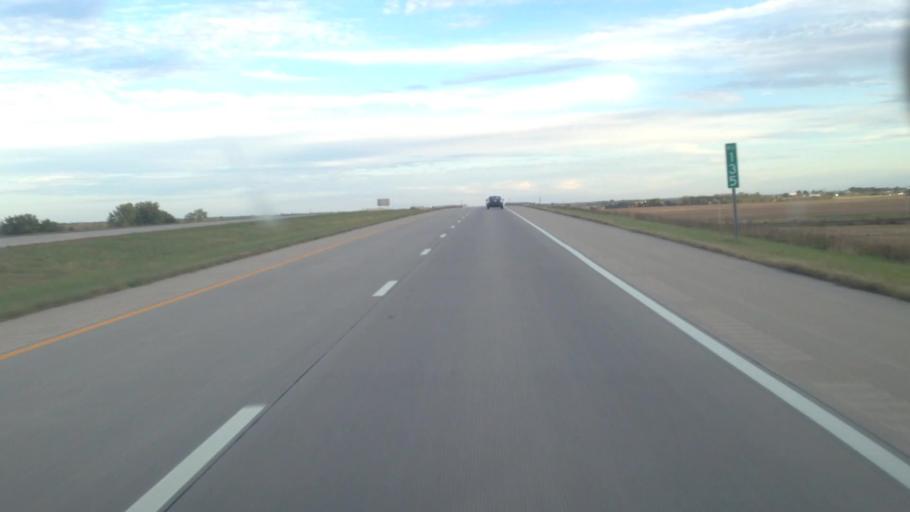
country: US
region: Kansas
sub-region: Franklin County
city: Ottawa
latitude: 38.6554
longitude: -95.2381
